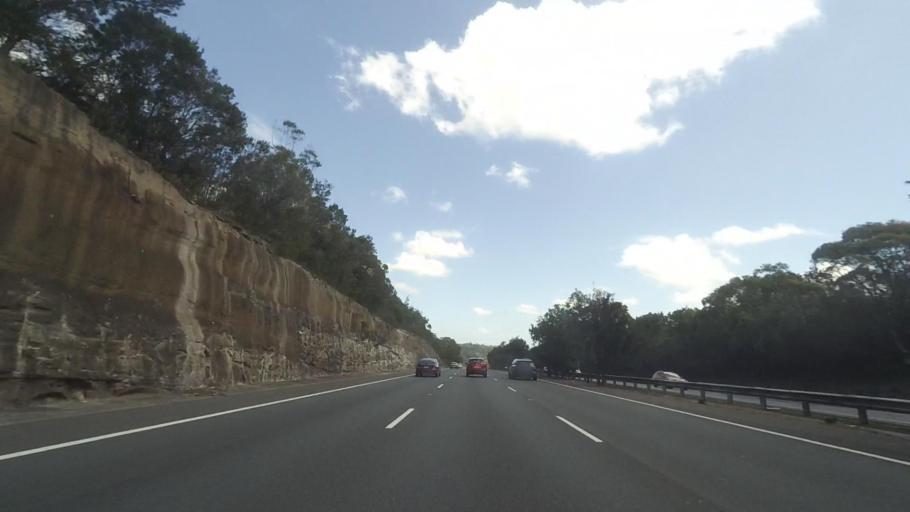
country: AU
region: New South Wales
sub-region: Hornsby Shire
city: Mount Colah
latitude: -33.6792
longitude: 151.1203
